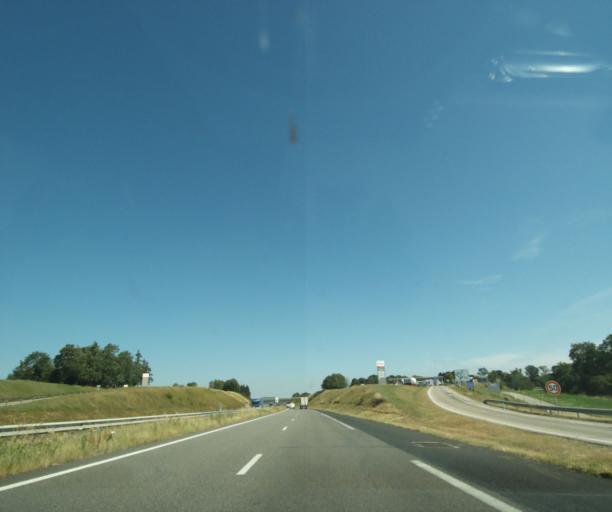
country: FR
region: Lorraine
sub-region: Departement des Vosges
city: Chatenois
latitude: 48.2644
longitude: 5.8638
